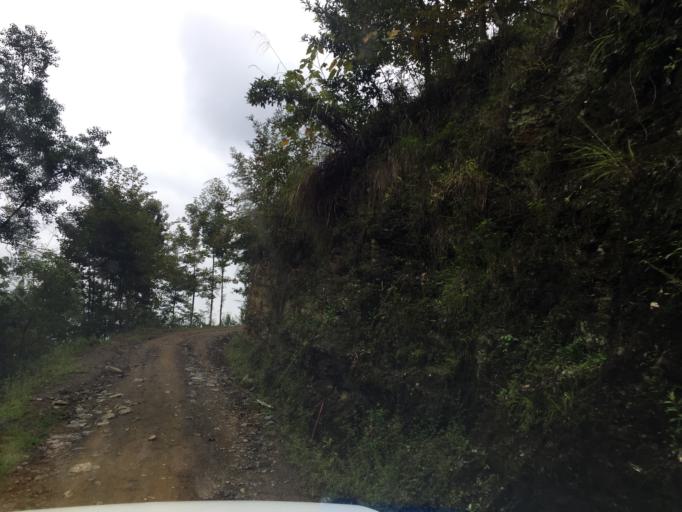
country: CN
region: Guizhou Sheng
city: Jingjiao
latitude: 28.3345
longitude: 108.1292
